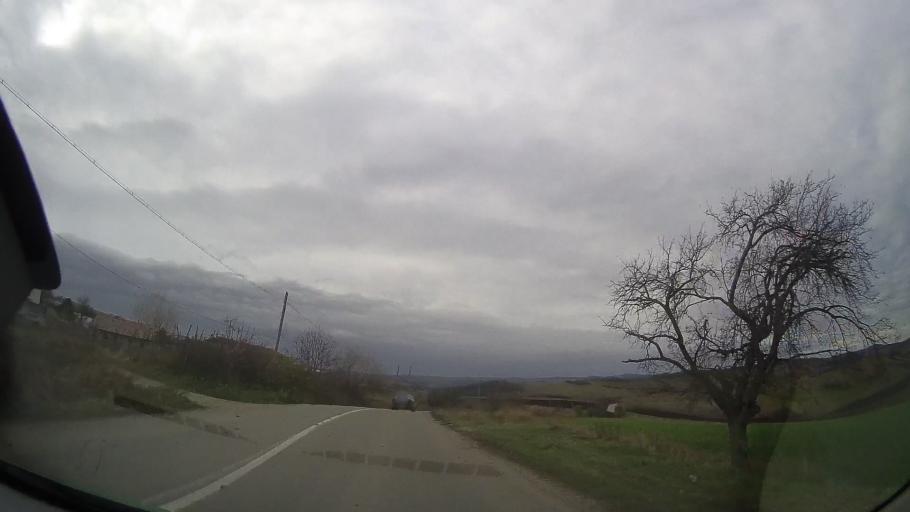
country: RO
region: Bistrita-Nasaud
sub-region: Comuna Milas
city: Milas
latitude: 46.8276
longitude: 24.4634
